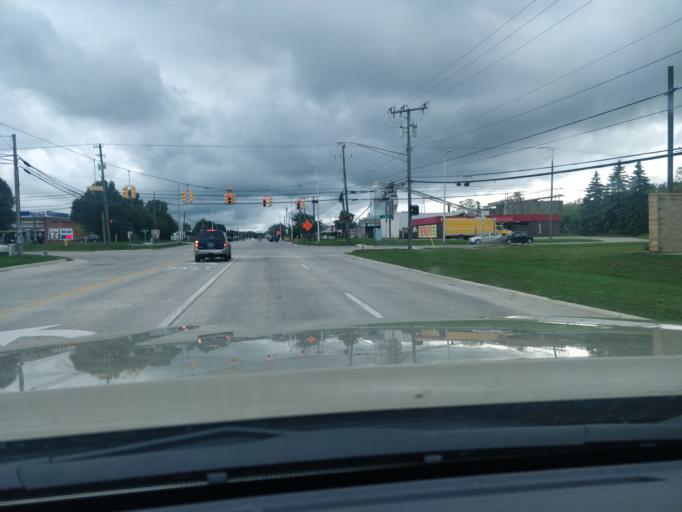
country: US
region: Michigan
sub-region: Wayne County
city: Woodhaven
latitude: 42.1697
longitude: -83.2264
